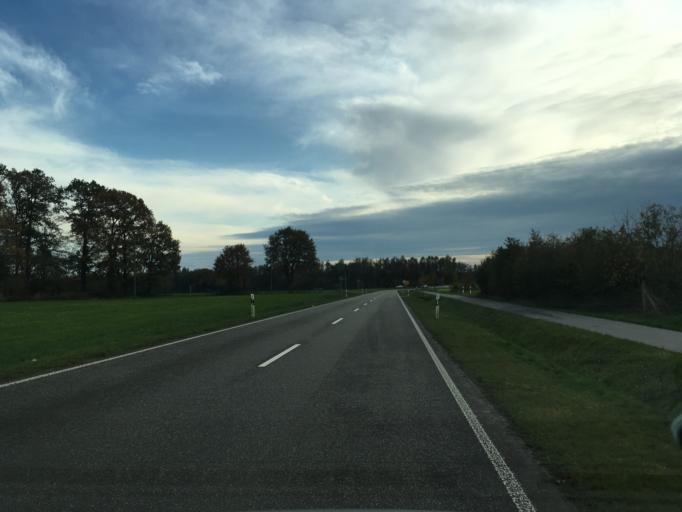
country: DE
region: North Rhine-Westphalia
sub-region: Regierungsbezirk Munster
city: Velen
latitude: 51.8945
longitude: 6.9280
